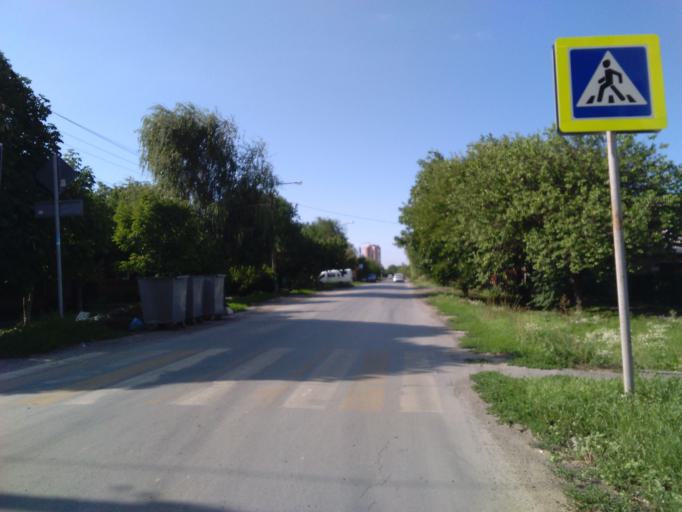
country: RU
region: Rostov
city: Bataysk
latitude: 47.1449
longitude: 39.7353
